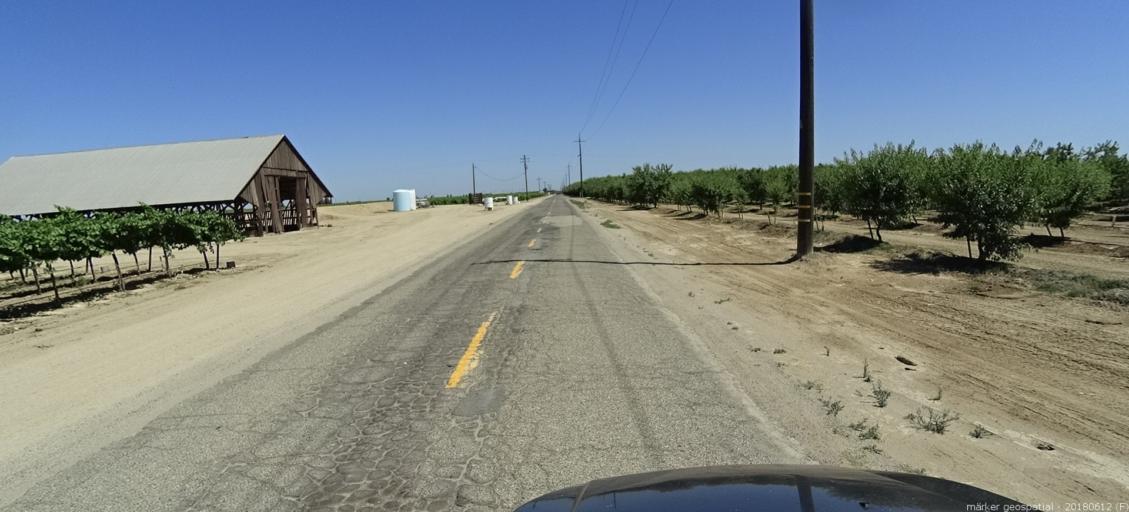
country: US
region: California
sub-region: Madera County
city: Chowchilla
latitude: 37.0241
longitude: -120.3286
